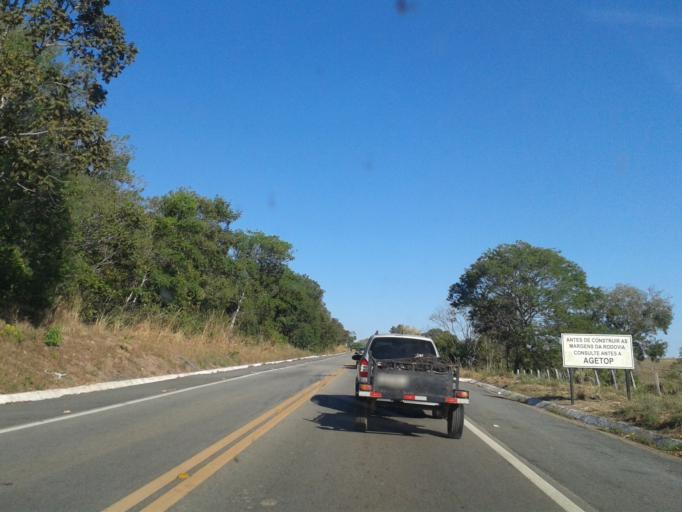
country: BR
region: Goias
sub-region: Mozarlandia
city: Mozarlandia
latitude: -15.1919
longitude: -50.5489
